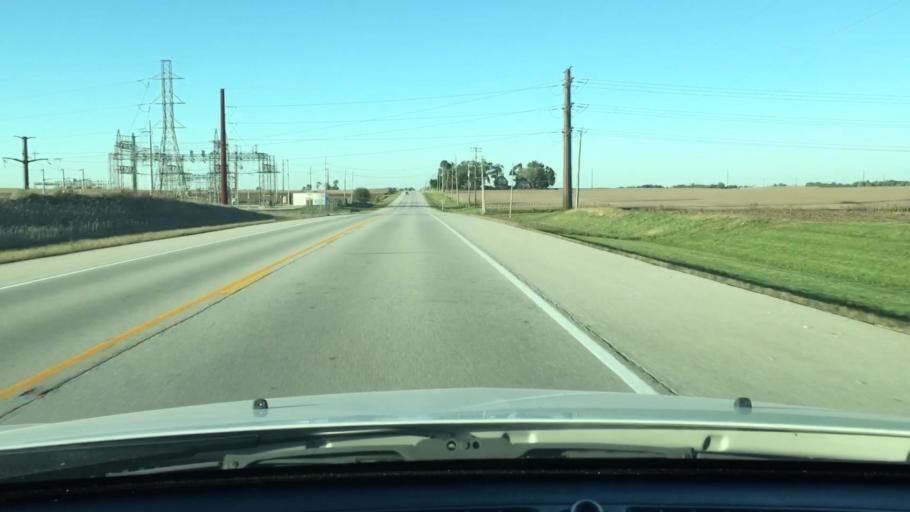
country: US
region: Illinois
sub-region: DeKalb County
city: Waterman
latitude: 41.8256
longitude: -88.7539
